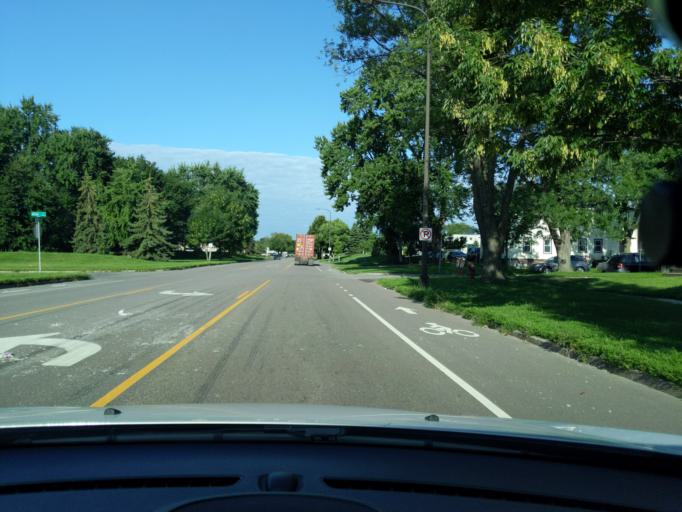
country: US
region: Minnesota
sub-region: Ramsey County
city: Falcon Heights
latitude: 44.9648
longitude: -93.1335
